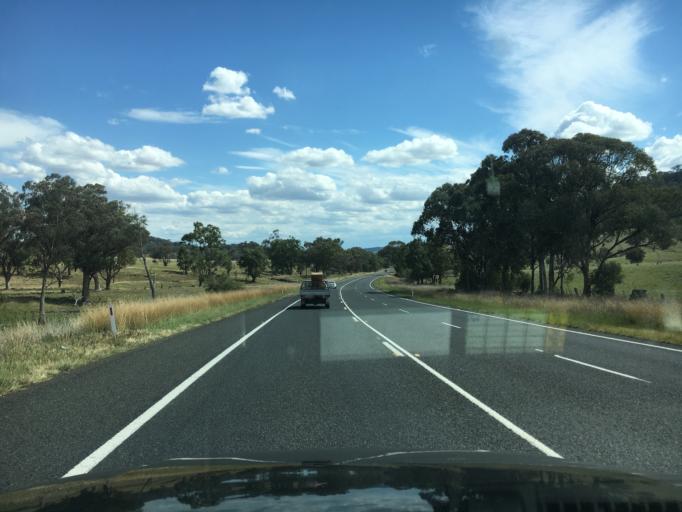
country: AU
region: New South Wales
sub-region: Liverpool Plains
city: Quirindi
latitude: -31.5085
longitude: 150.8596
